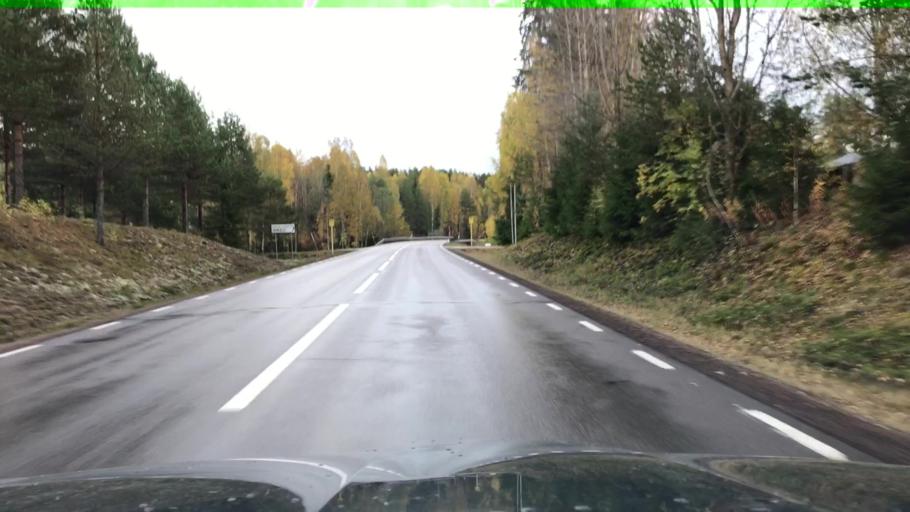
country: SE
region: Vaermland
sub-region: Hagfors Kommun
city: Ekshaerad
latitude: 60.4298
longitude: 13.2436
